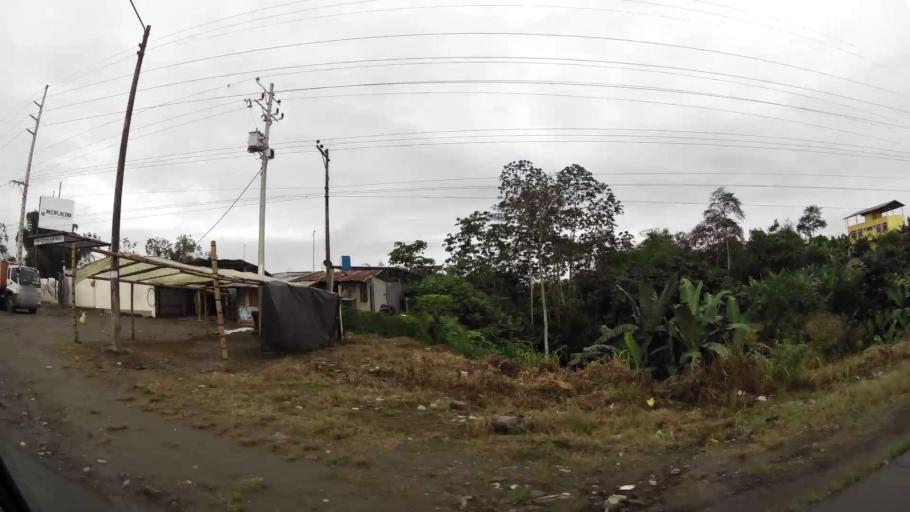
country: EC
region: Santo Domingo de los Tsachilas
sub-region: Canton Santo Domingo de los Colorados
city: Santo Domingo de los Colorados
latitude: -0.2644
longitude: -79.2025
